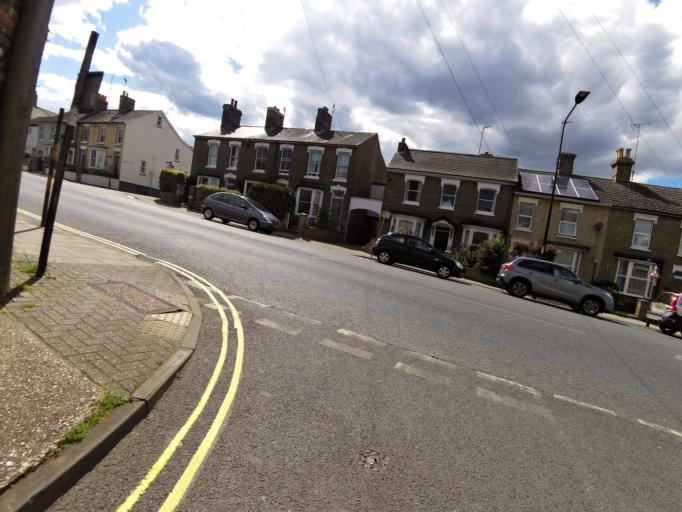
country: GB
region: England
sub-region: Suffolk
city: Bury St Edmunds
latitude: 52.2500
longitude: 0.7114
